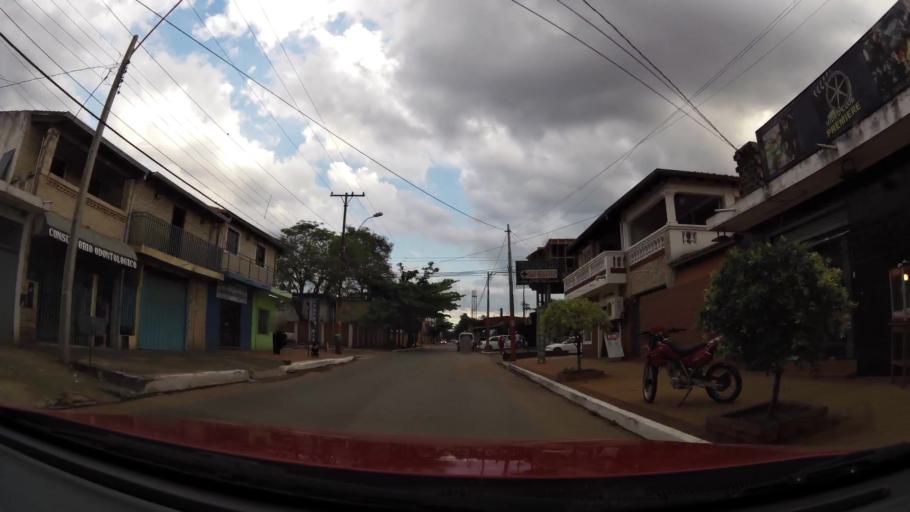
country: PY
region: Central
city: Fernando de la Mora
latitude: -25.3305
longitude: -57.5519
